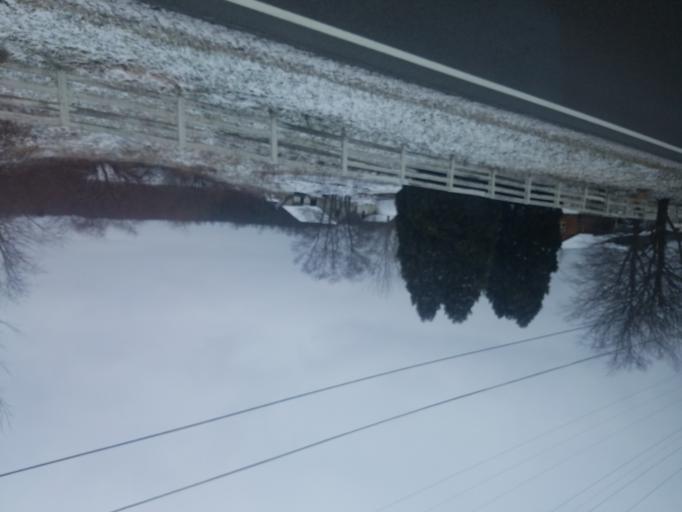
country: US
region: Ohio
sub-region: Licking County
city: Johnstown
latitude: 40.1713
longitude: -82.7154
